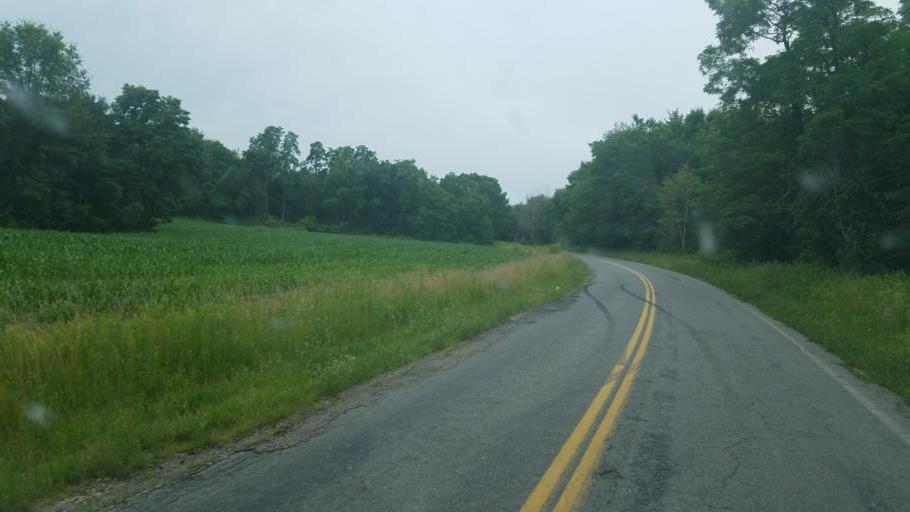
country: US
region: Ohio
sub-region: Trumbull County
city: South Canal
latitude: 41.1865
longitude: -81.0218
